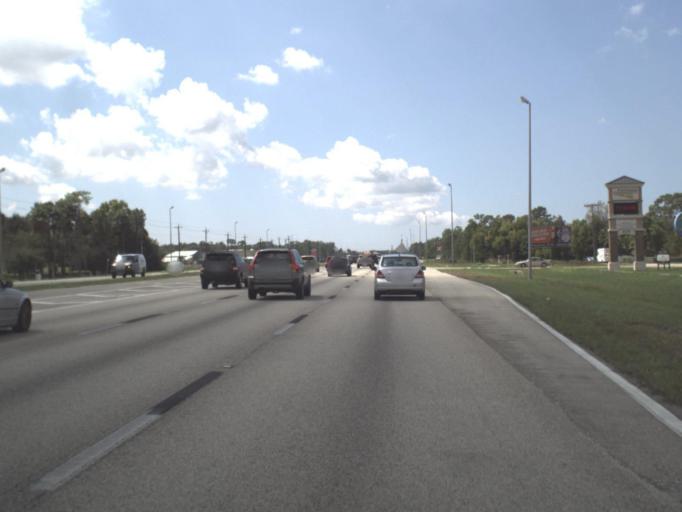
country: US
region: Florida
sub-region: Lee County
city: Fort Myers
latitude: 26.6076
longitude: -81.8240
